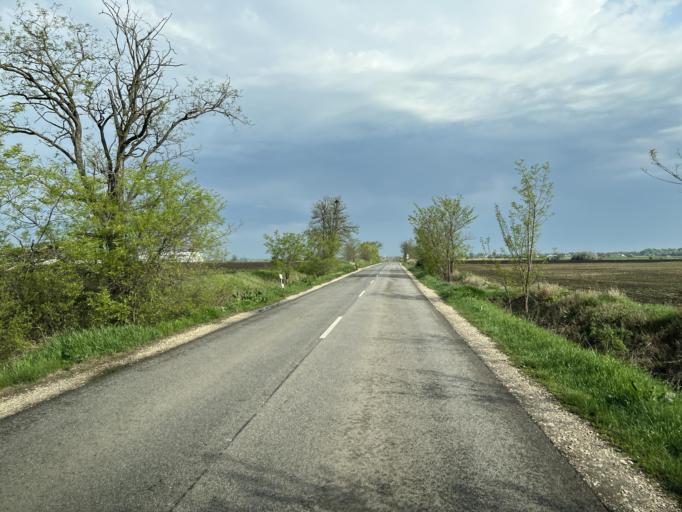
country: HU
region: Pest
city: Tapioszentmarton
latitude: 47.3118
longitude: 19.7593
